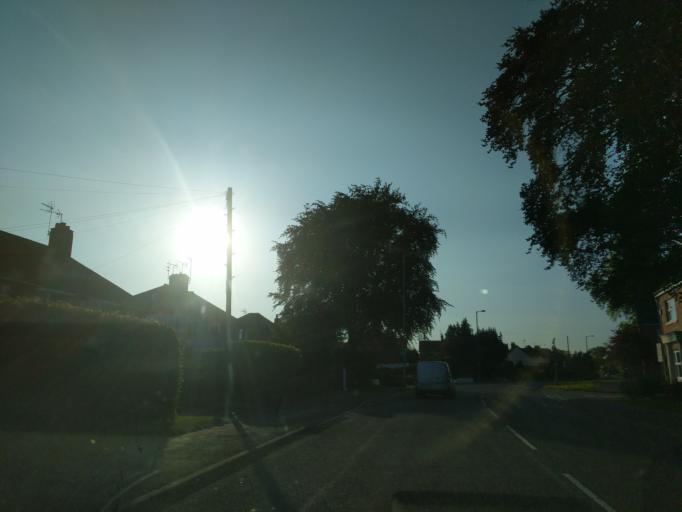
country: GB
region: England
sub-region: Staffordshire
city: Stone
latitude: 52.8959
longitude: -2.1343
